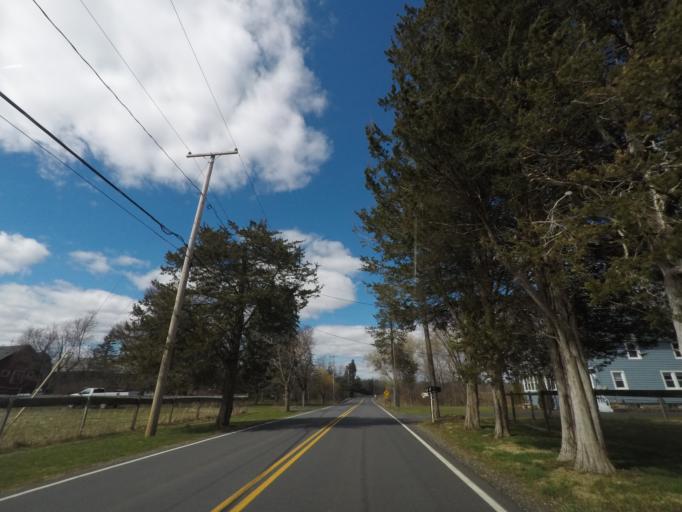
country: US
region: New York
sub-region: Albany County
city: Delmar
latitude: 42.5666
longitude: -73.8253
